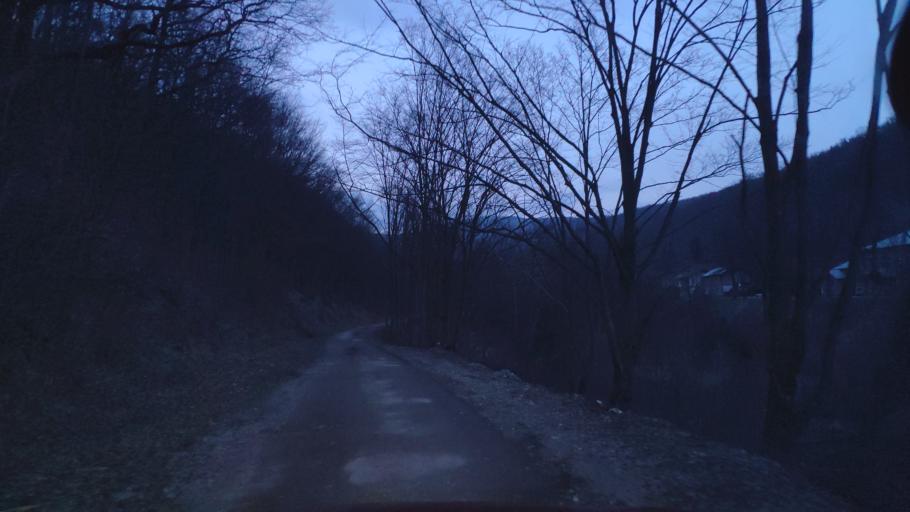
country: SK
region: Kosicky
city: Medzev
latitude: 48.7205
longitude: 20.9252
